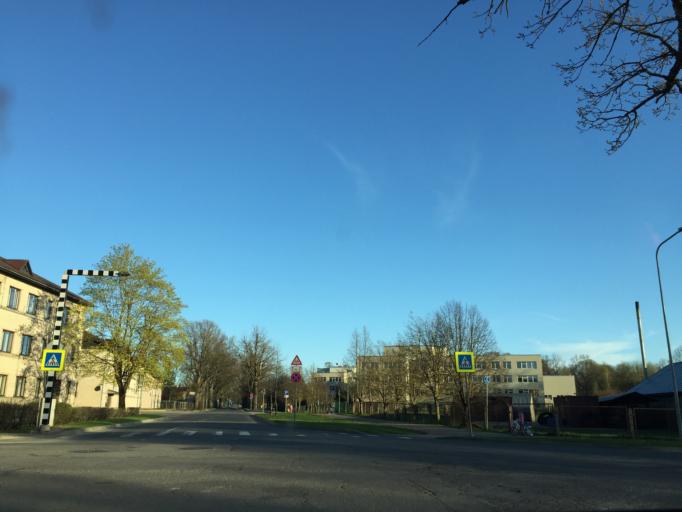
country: LV
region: Valmieras Rajons
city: Valmiera
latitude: 57.5478
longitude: 25.4221
